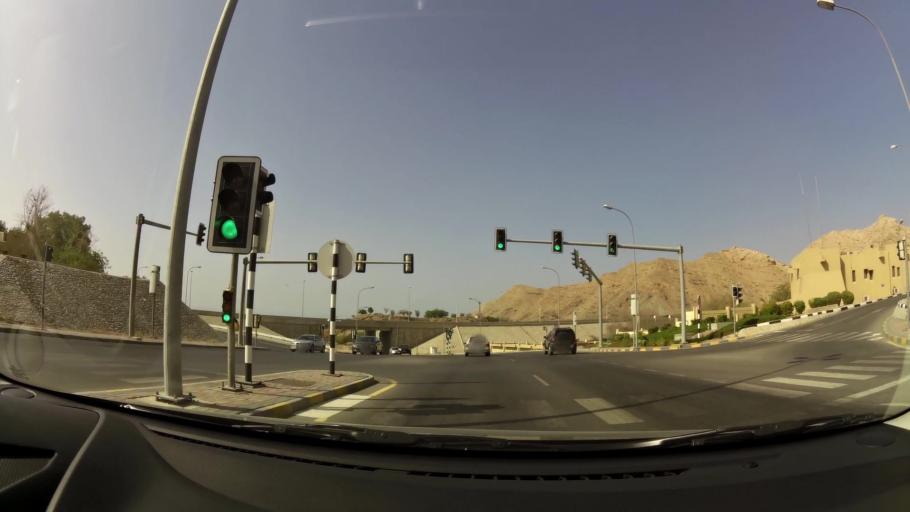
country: OM
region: Muhafazat Masqat
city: Muscat
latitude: 23.6171
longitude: 58.5192
